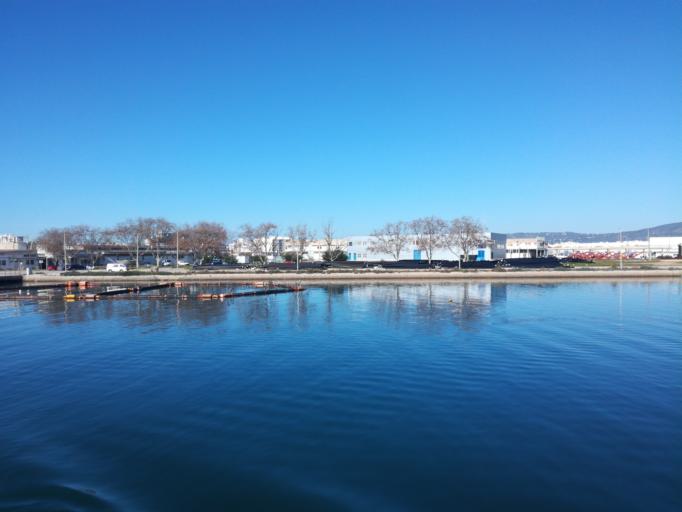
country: PT
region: Faro
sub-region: Olhao
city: Olhao
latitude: 37.0237
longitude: -7.8319
